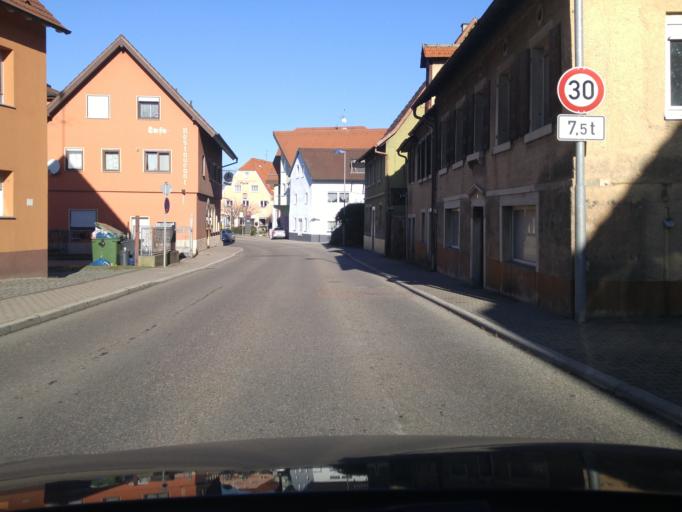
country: DE
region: Baden-Wuerttemberg
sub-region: Karlsruhe Region
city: Sinsheim
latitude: 49.2381
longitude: 8.9109
